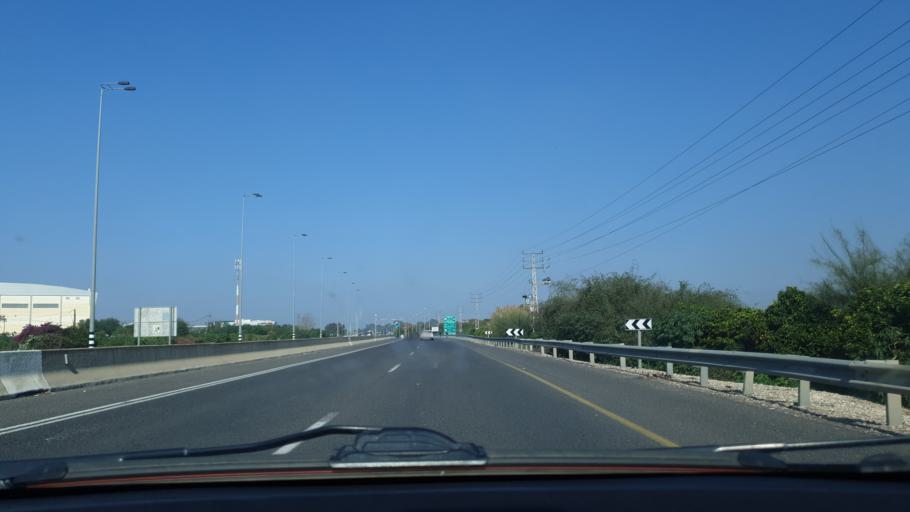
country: IL
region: Central District
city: Ramla
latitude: 31.9559
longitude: 34.8544
